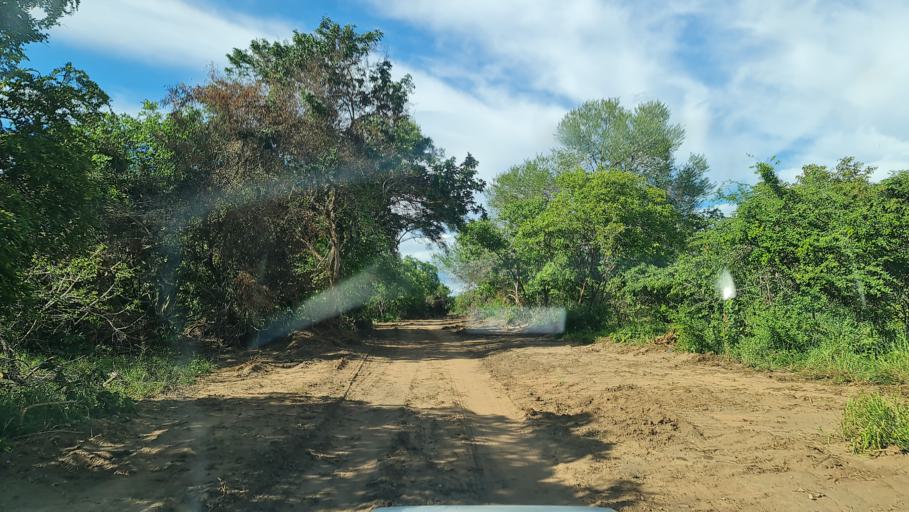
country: MZ
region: Nampula
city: Antonio Enes
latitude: -15.5179
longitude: 40.1295
